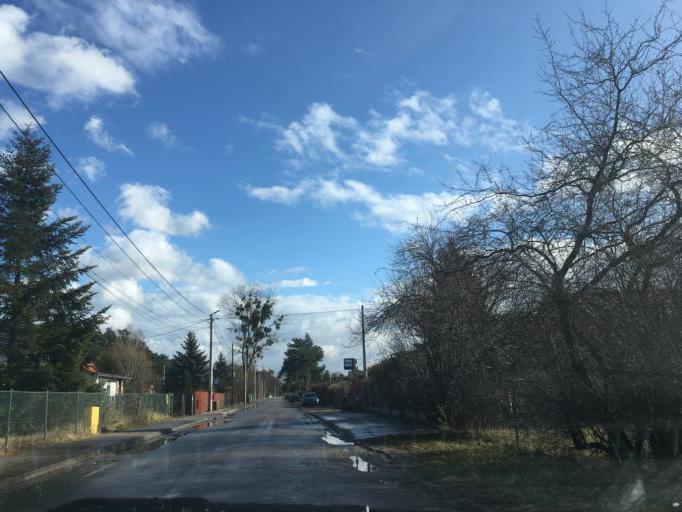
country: PL
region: Pomeranian Voivodeship
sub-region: Powiat gdanski
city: Cedry Wielkie
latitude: 54.3490
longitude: 18.8031
